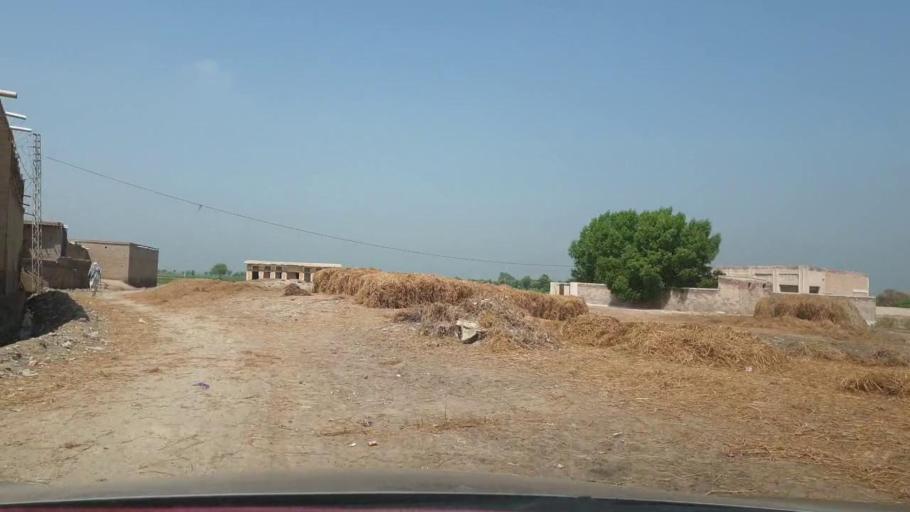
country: PK
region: Sindh
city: Kambar
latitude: 27.5910
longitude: 67.9096
